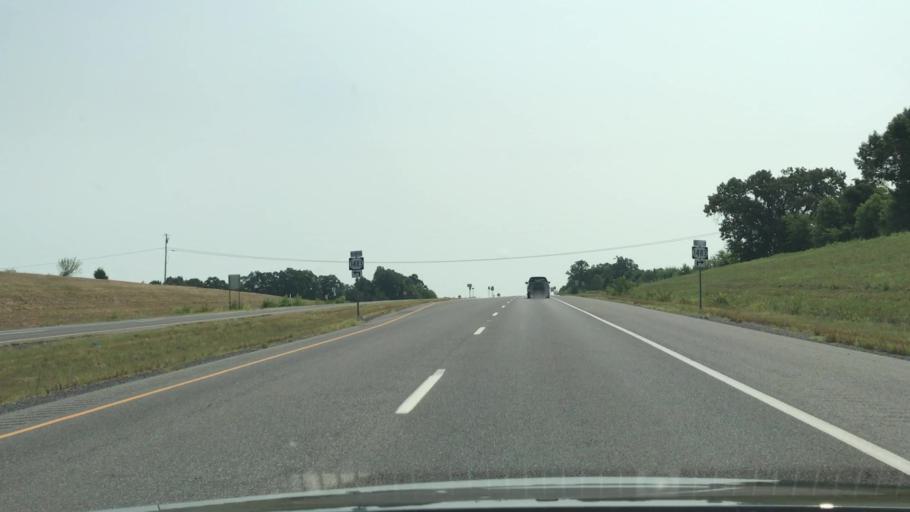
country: US
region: Kentucky
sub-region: Calloway County
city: Murray
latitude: 36.6512
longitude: -88.2741
